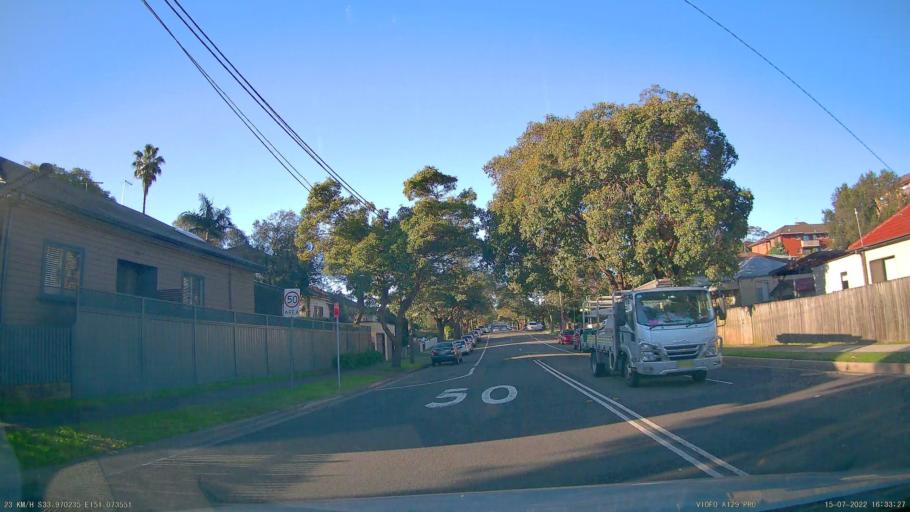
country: AU
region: New South Wales
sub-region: Hurstville
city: Oatley
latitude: -33.9702
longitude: 151.0737
